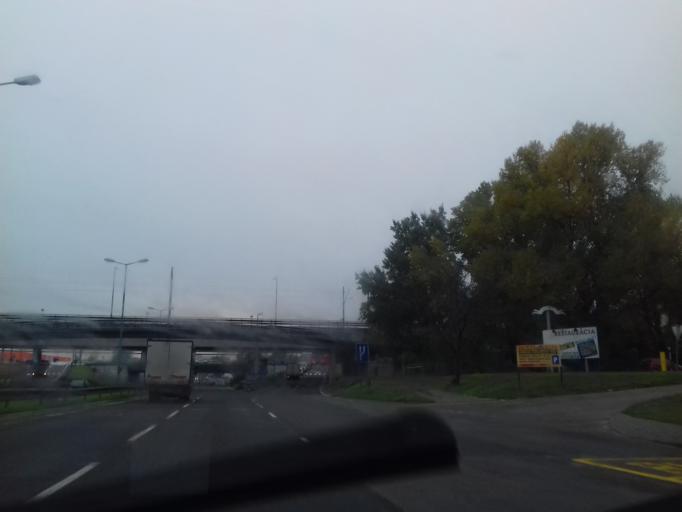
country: SK
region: Bratislavsky
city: Bratislava
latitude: 48.1394
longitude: 17.1525
